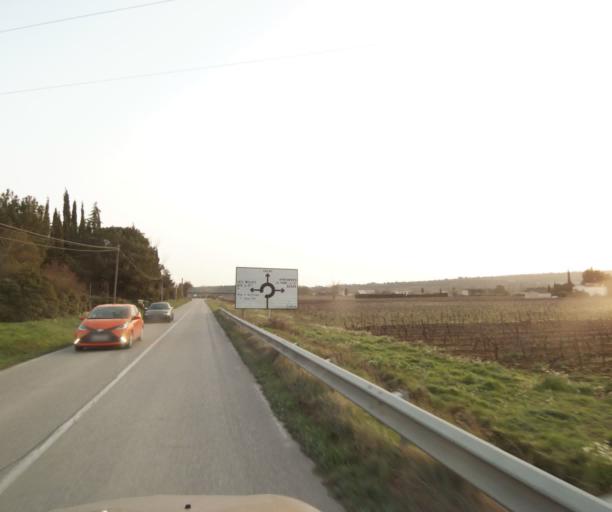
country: FR
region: Provence-Alpes-Cote d'Azur
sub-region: Departement des Bouches-du-Rhone
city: Eguilles
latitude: 43.5473
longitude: 5.3488
